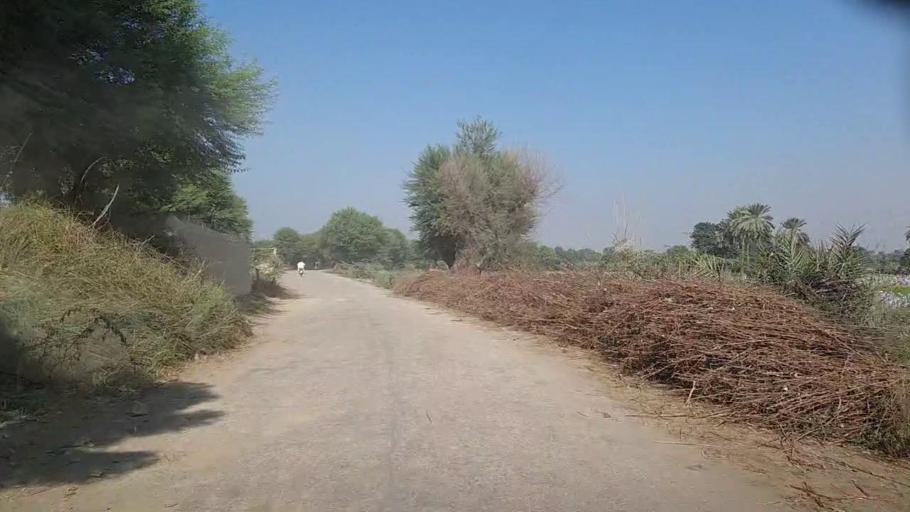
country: PK
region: Sindh
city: Bozdar
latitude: 27.2007
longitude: 68.6652
